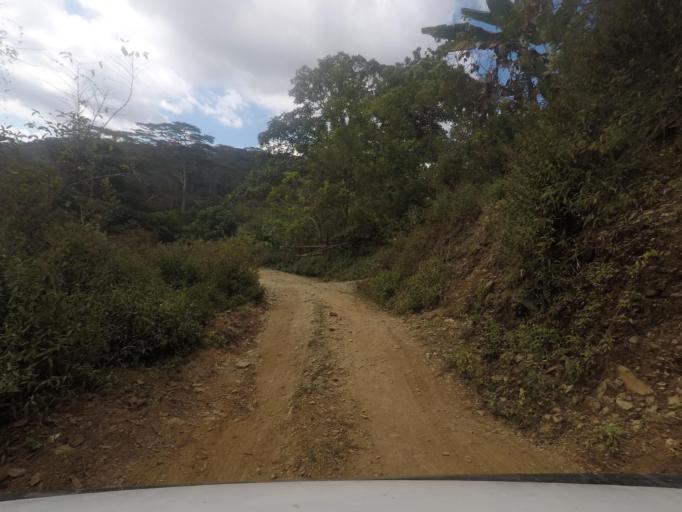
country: TL
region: Ermera
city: Gleno
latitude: -8.7492
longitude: 125.3220
